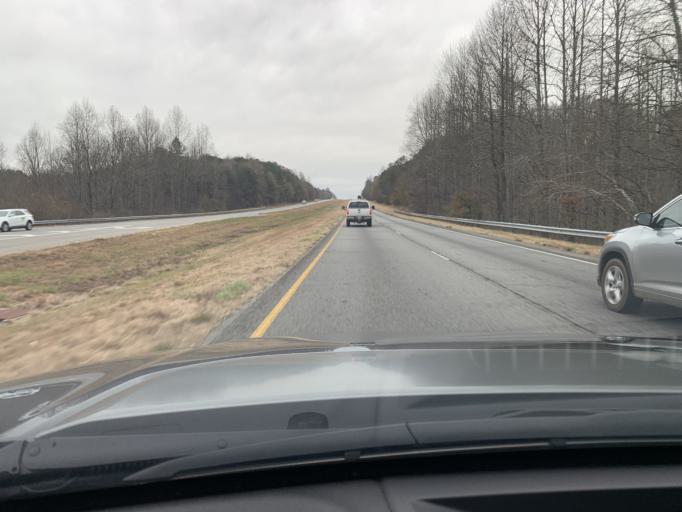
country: US
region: Georgia
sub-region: Hall County
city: Lula
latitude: 34.4144
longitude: -83.6598
